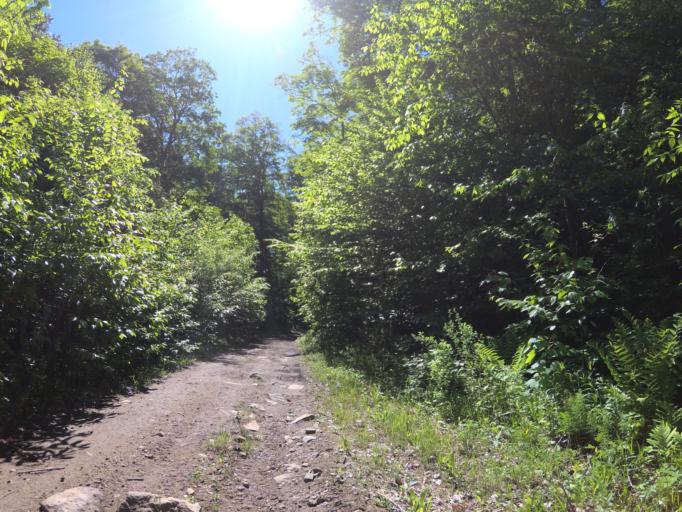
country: CA
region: Ontario
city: Renfrew
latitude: 45.0712
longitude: -77.0774
